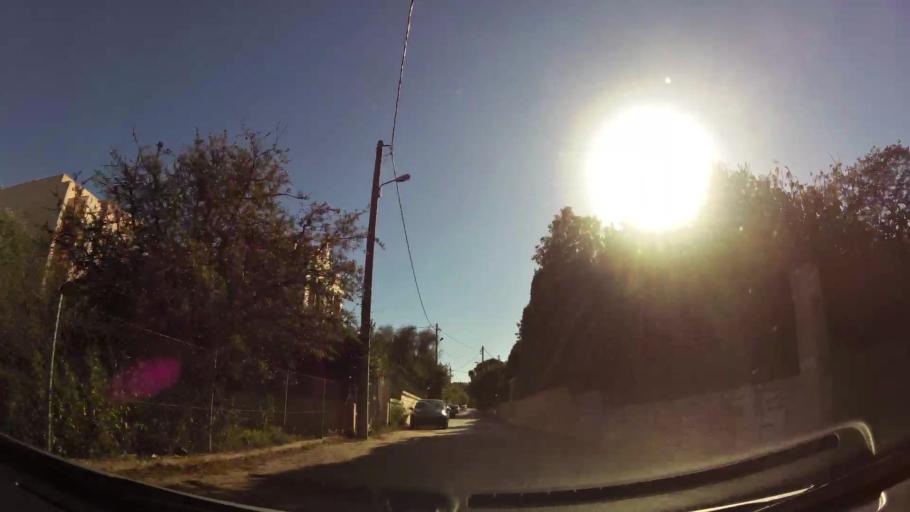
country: GR
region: Attica
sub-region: Nomarchia Athinas
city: Nea Erythraia
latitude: 38.0978
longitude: 23.8163
